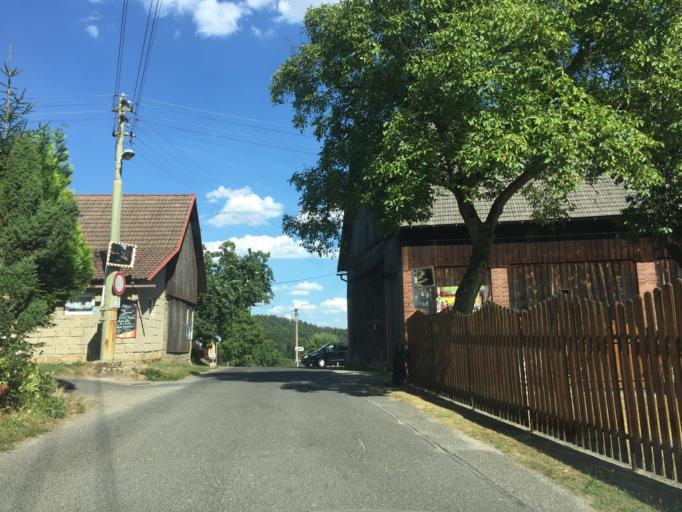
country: CZ
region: Liberecky
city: Mala Skala
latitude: 50.6276
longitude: 15.2109
